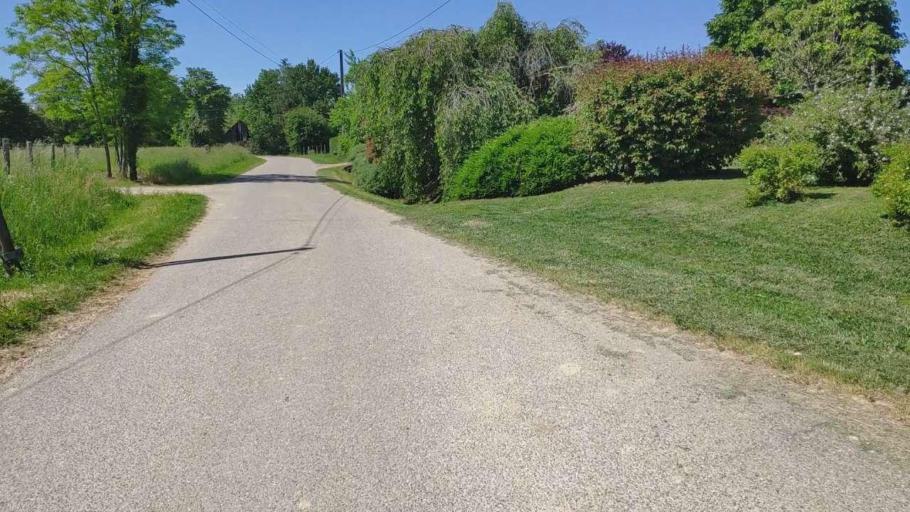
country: FR
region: Franche-Comte
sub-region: Departement du Jura
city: Bletterans
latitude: 46.7764
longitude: 5.4144
